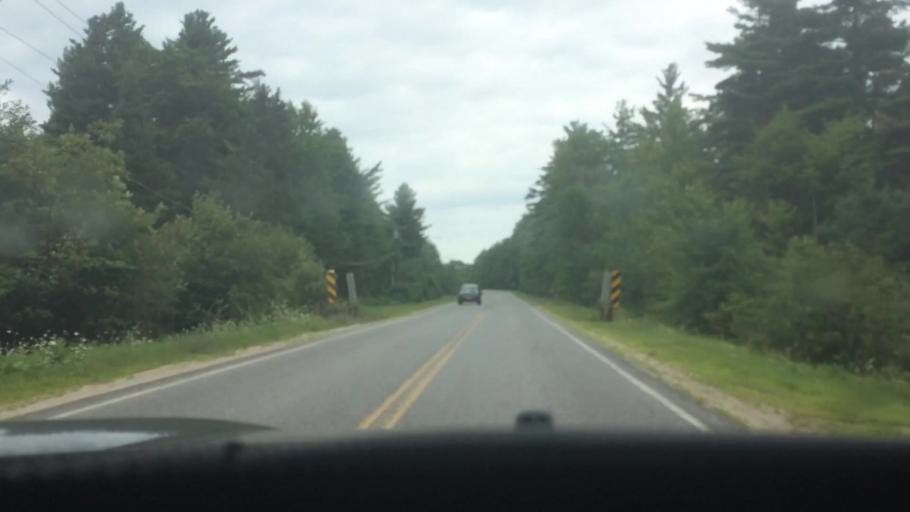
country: US
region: New York
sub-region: St. Lawrence County
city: Hannawa Falls
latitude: 44.5478
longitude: -74.9305
